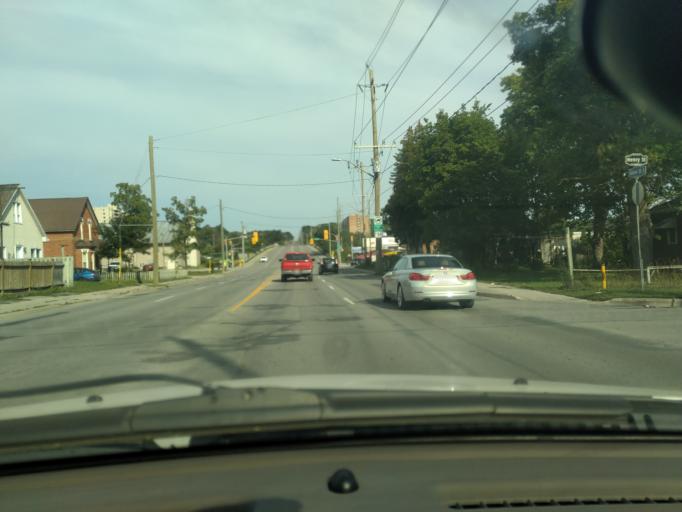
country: CA
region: Ontario
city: Barrie
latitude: 44.3835
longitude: -79.7060
